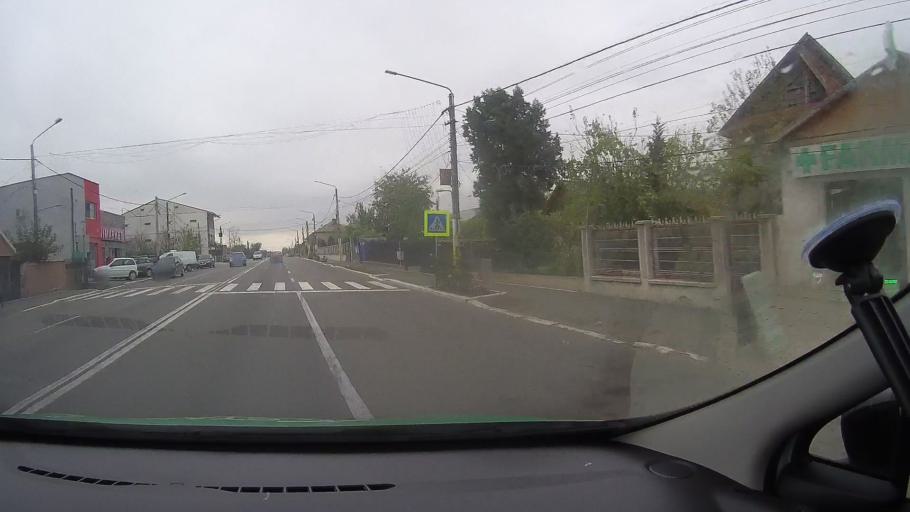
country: RO
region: Constanta
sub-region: Comuna Valu lui Traian
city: Valu lui Traian
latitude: 44.1661
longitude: 28.4627
